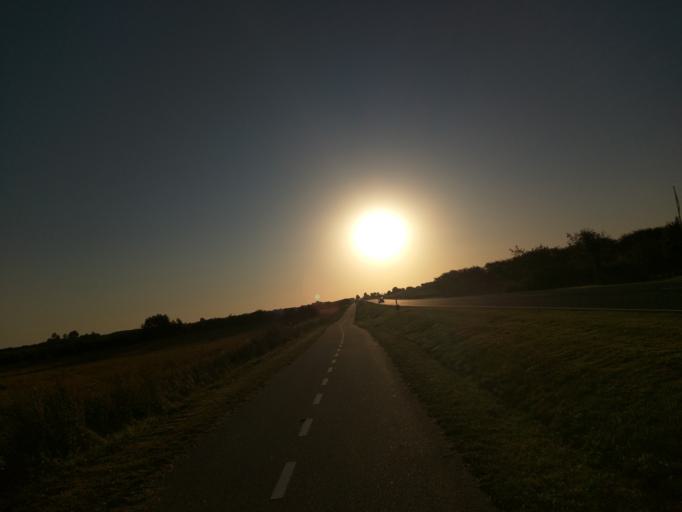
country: DK
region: Central Jutland
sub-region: Viborg Kommune
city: Viborg
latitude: 56.4602
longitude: 9.4753
